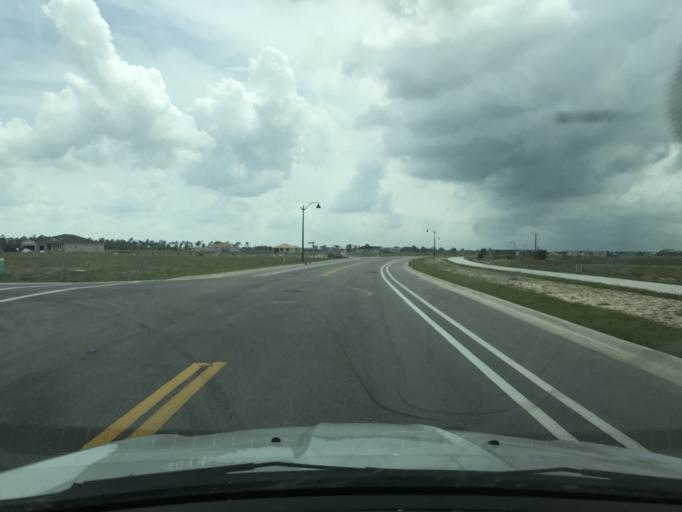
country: US
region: Florida
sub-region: Lee County
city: Olga
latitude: 26.7902
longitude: -81.7350
